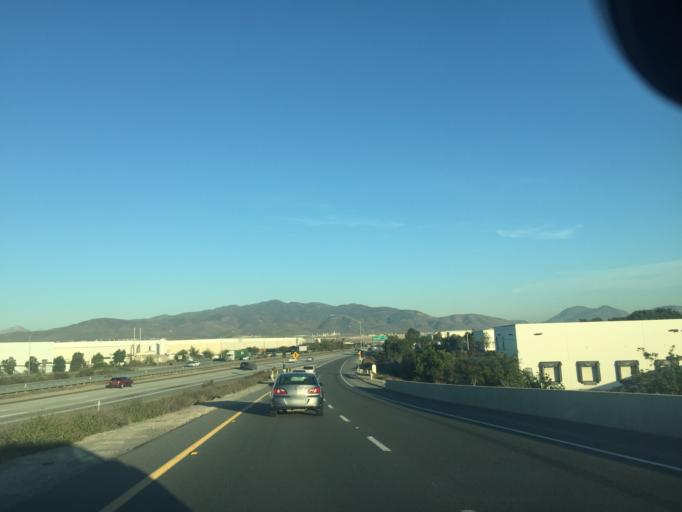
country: MX
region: Baja California
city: Tijuana
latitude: 32.5638
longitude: -116.9791
